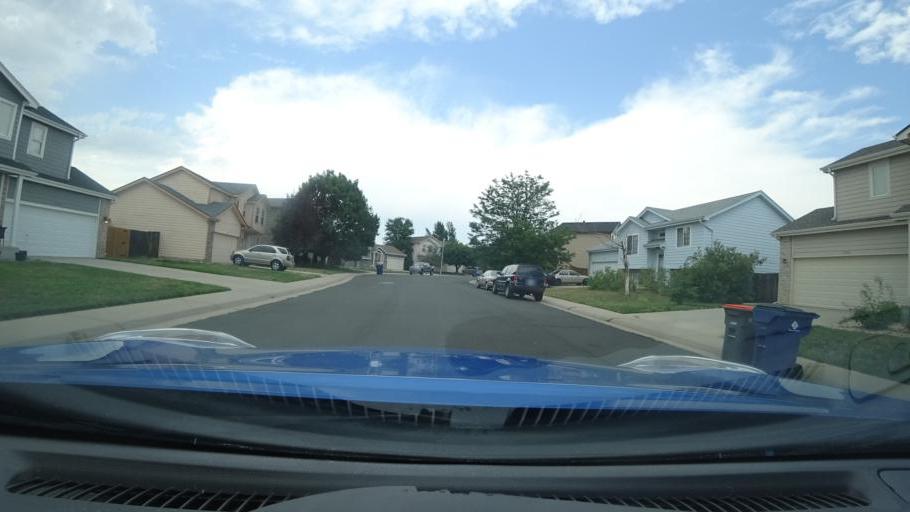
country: US
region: Colorado
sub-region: Adams County
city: Aurora
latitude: 39.6907
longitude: -104.7871
